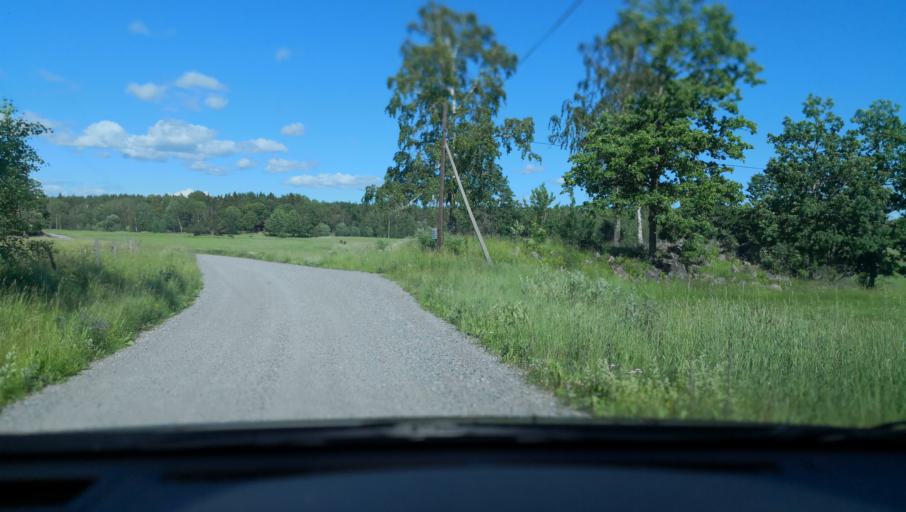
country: SE
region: Soedermanland
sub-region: Eskilstuna Kommun
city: Hallbybrunn
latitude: 59.3033
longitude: 16.3621
